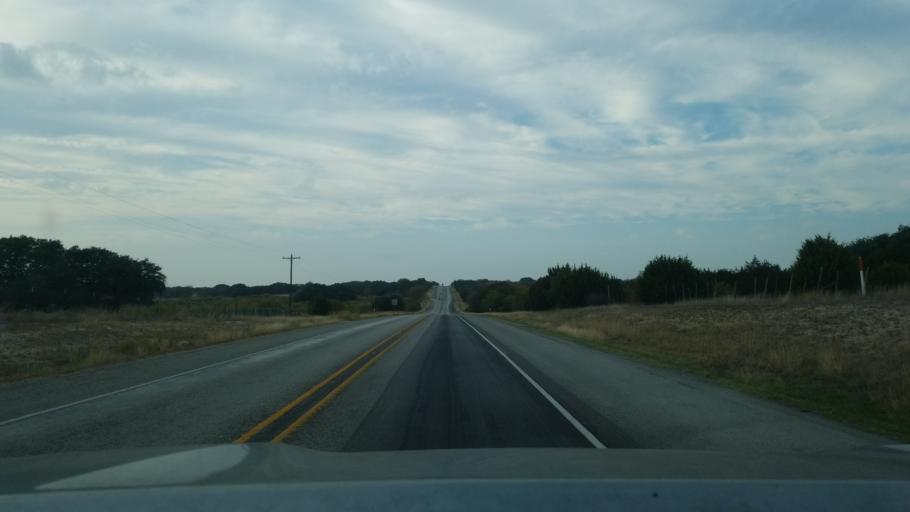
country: US
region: Texas
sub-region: Mills County
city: Goldthwaite
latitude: 31.5319
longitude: -98.6126
